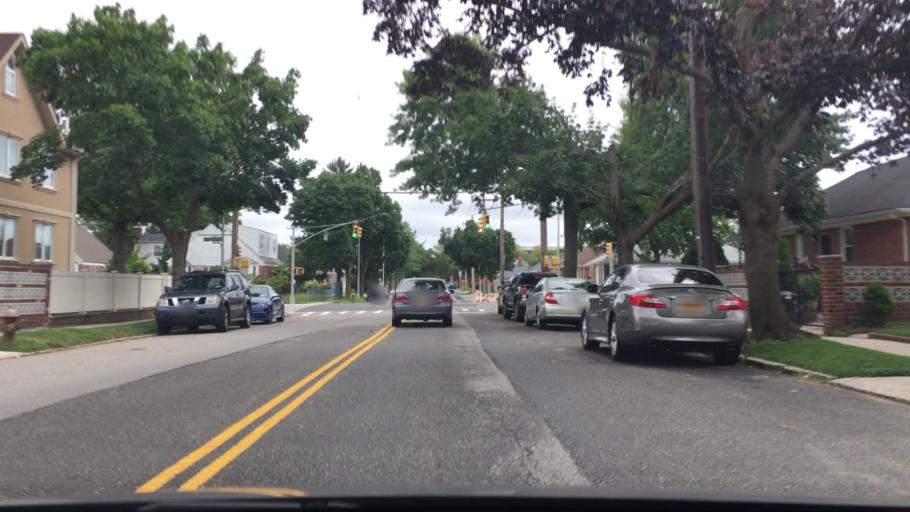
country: US
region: New York
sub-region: Nassau County
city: Bellerose
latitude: 40.7415
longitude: -73.7172
